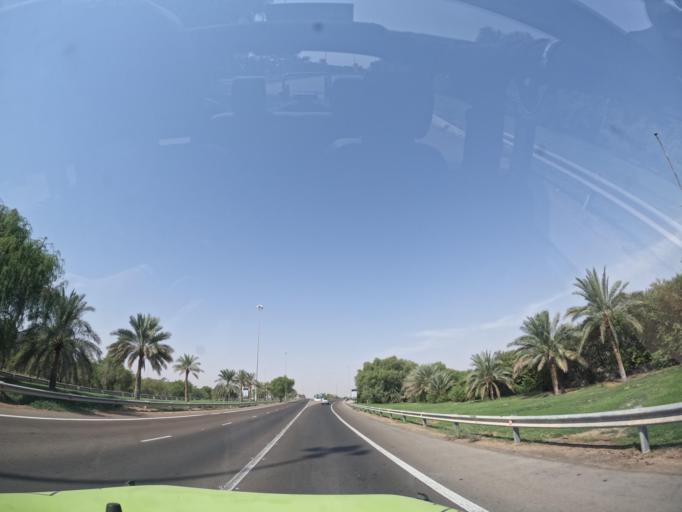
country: AE
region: Abu Dhabi
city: Al Ain
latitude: 24.2003
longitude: 55.5883
